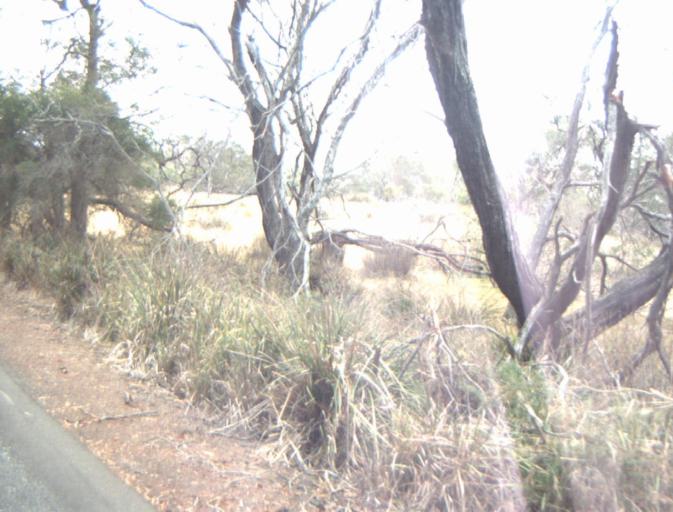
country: AU
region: Tasmania
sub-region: Launceston
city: Mayfield
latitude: -41.2828
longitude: 147.0272
